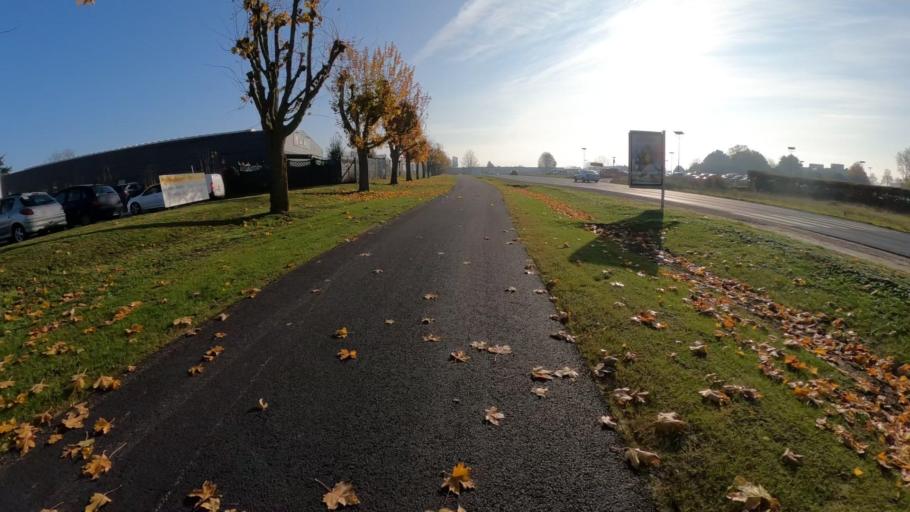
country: FR
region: Lower Normandy
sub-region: Departement du Calvados
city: Epron
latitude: 49.2087
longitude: -0.3508
